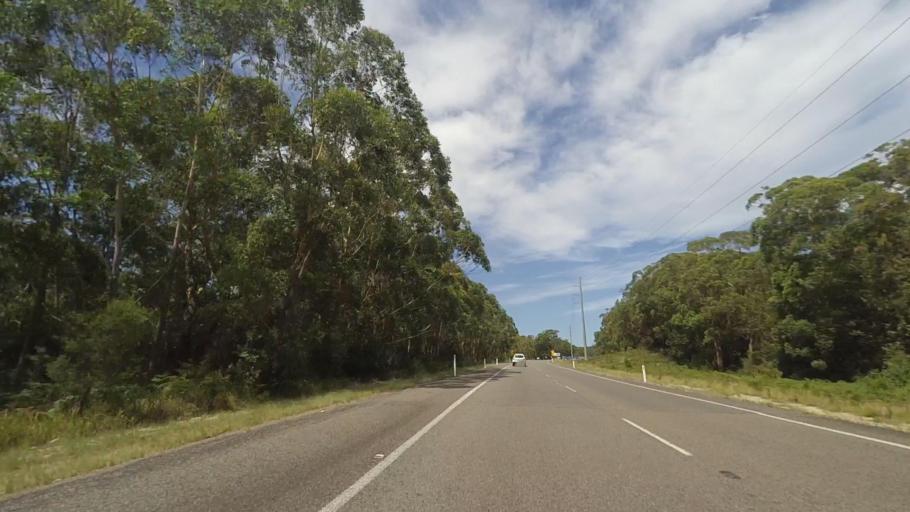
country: AU
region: New South Wales
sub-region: Port Stephens Shire
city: Medowie
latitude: -32.7863
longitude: 151.9673
